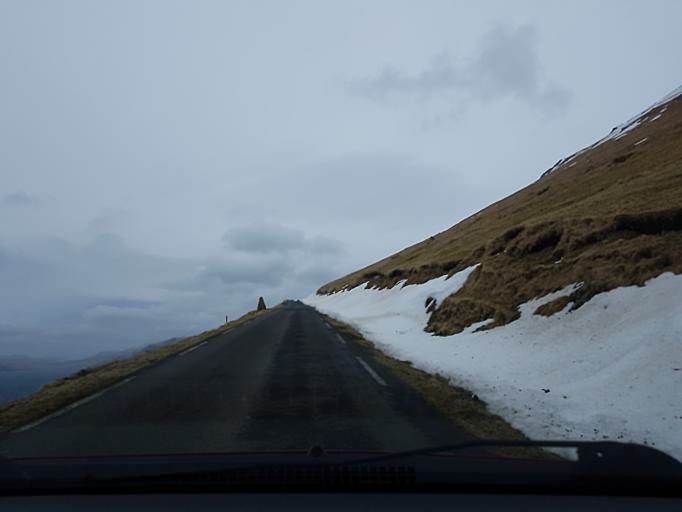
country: FO
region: Streymoy
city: Kollafjordhur
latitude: 62.0021
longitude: -6.9028
